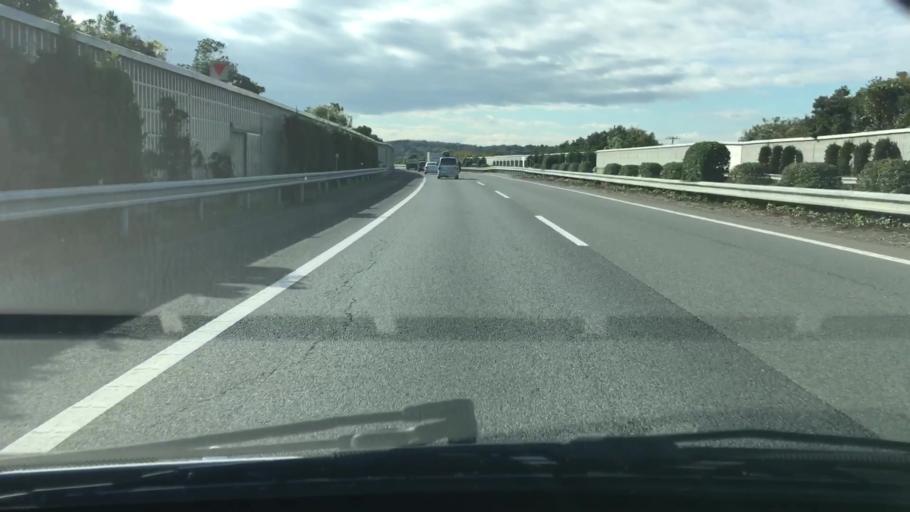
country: JP
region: Chiba
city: Ichihara
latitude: 35.4855
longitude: 140.0828
